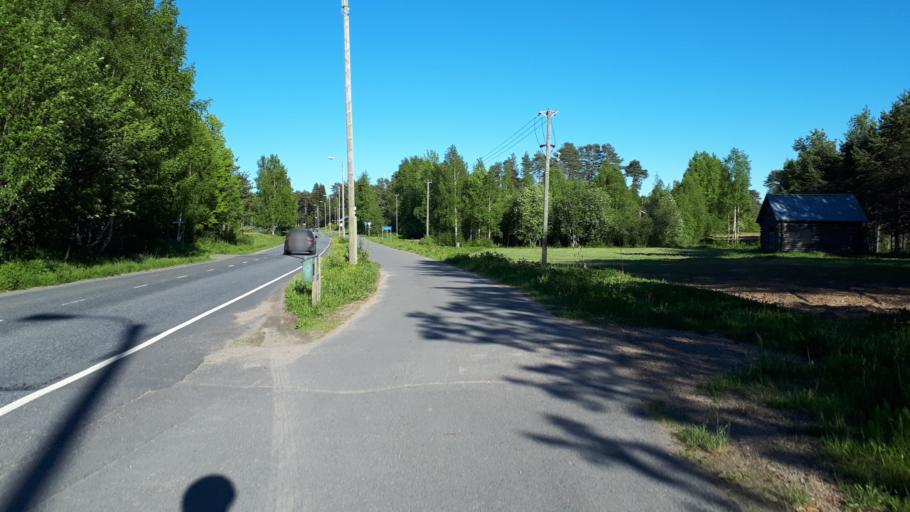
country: FI
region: Northern Ostrobothnia
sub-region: Oulunkaari
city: Ii
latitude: 65.3228
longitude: 25.4533
